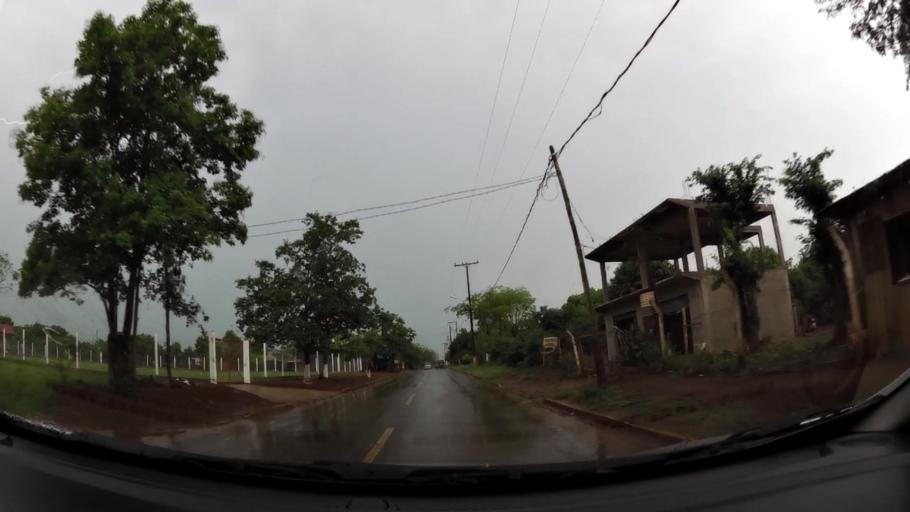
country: PY
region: Alto Parana
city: Presidente Franco
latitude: -25.5506
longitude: -54.6701
